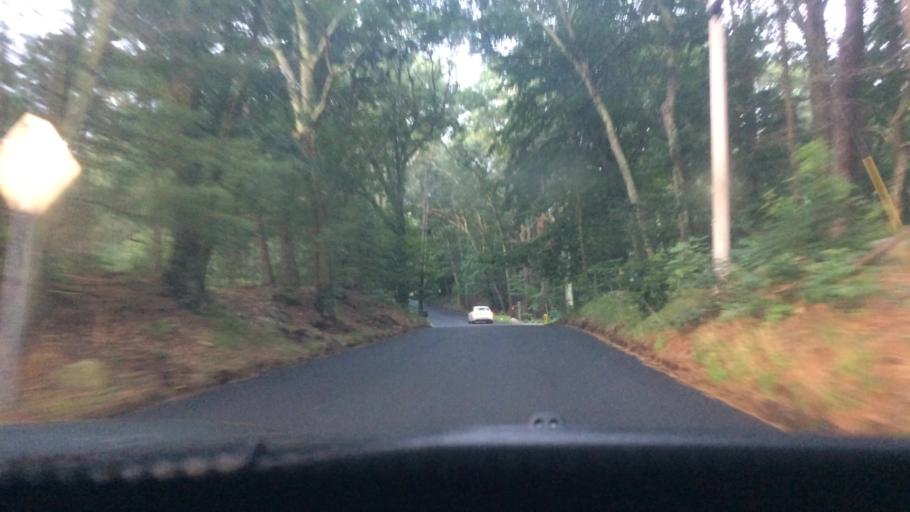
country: US
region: Massachusetts
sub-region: Middlesex County
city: North Reading
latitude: 42.6221
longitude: -71.0942
